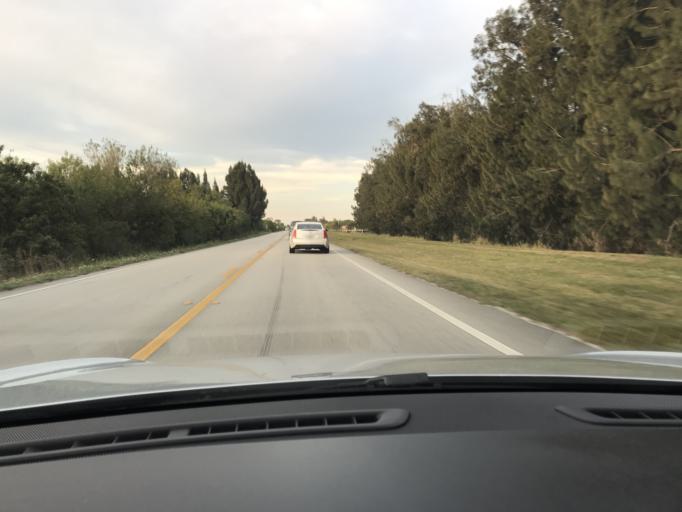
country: US
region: Florida
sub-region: Saint Lucie County
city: Lakewood Park
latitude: 27.5637
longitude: -80.4309
